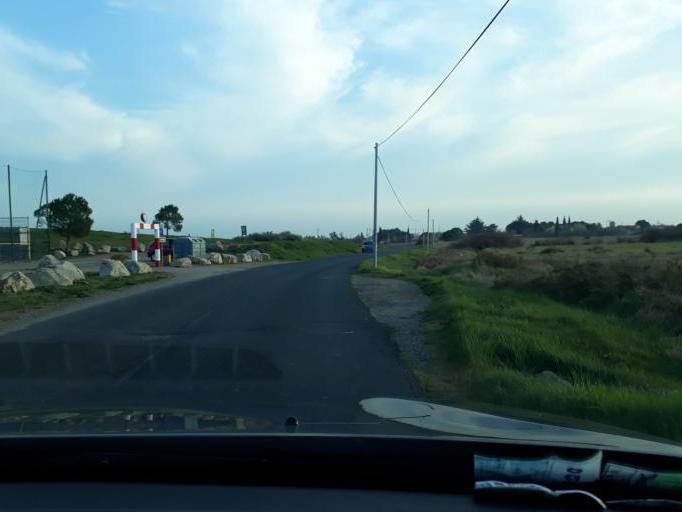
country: FR
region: Languedoc-Roussillon
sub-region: Departement de l'Herault
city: Marseillan
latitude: 43.3344
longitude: 3.5316
